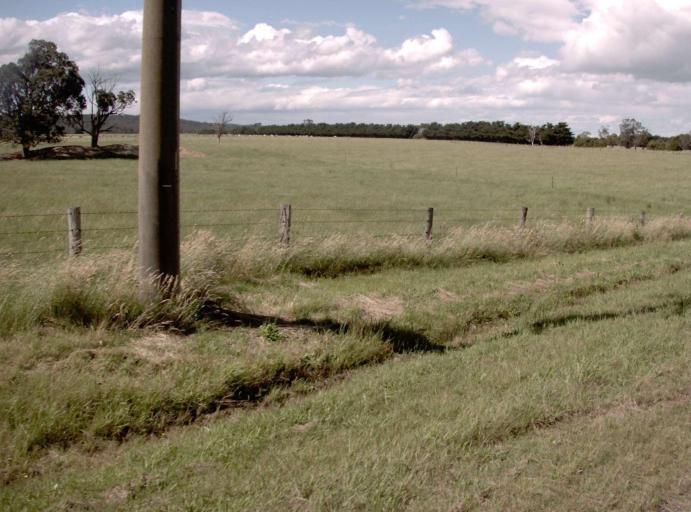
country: AU
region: Victoria
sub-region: Latrobe
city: Traralgon
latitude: -38.1362
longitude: 146.5423
